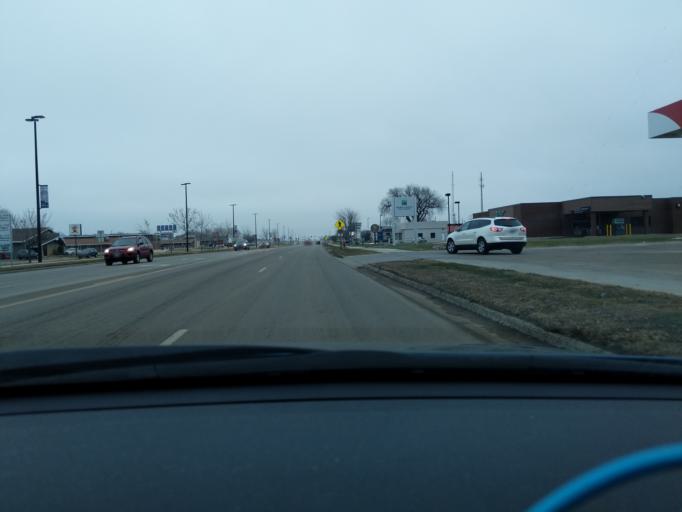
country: US
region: Minnesota
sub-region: Lyon County
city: Marshall
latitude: 44.4504
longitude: -95.7642
